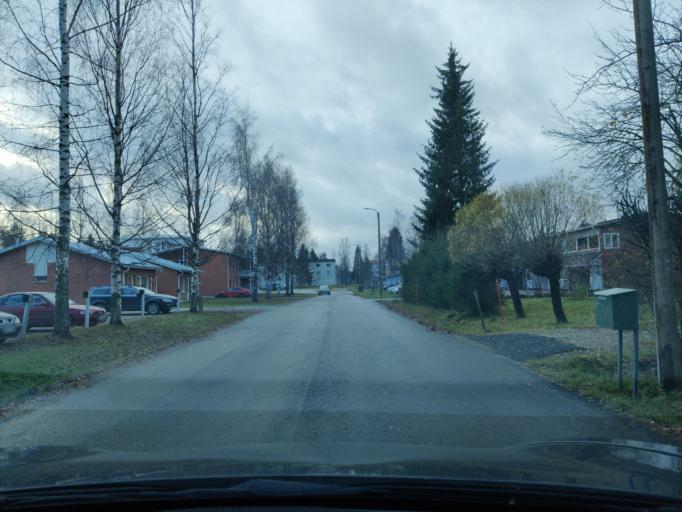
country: FI
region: Northern Savo
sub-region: Ylae-Savo
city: Kiuruvesi
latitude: 63.6472
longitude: 26.6344
